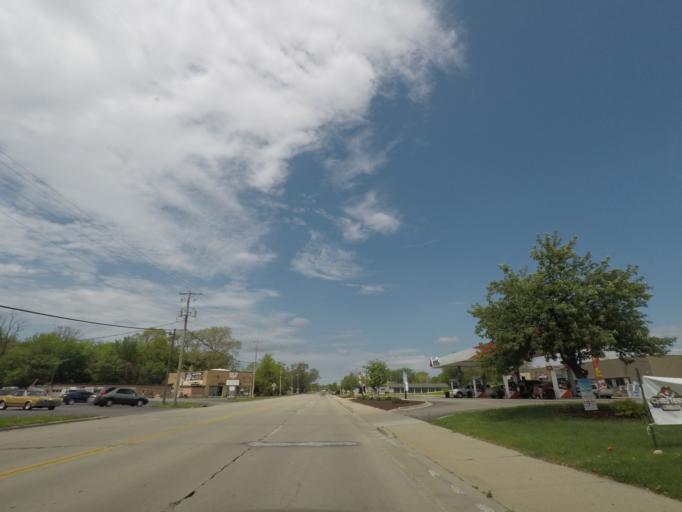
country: US
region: Wisconsin
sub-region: Rock County
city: Beloit
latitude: 42.5154
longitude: -89.0616
